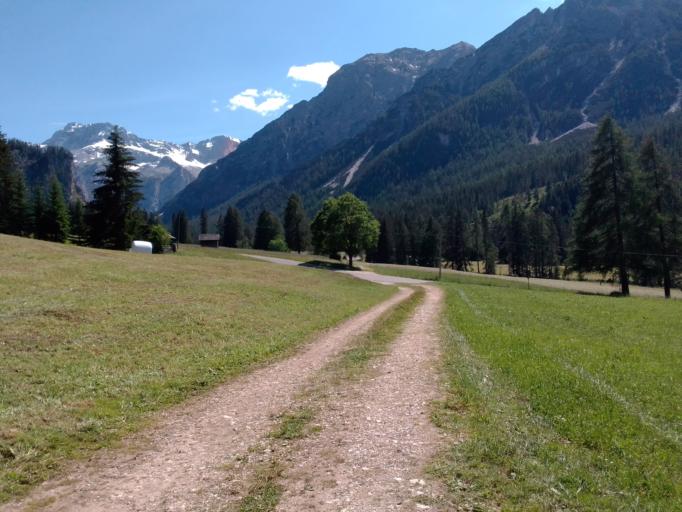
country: IT
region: Trentino-Alto Adige
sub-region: Bolzano
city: Braies
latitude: 46.7055
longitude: 12.1555
